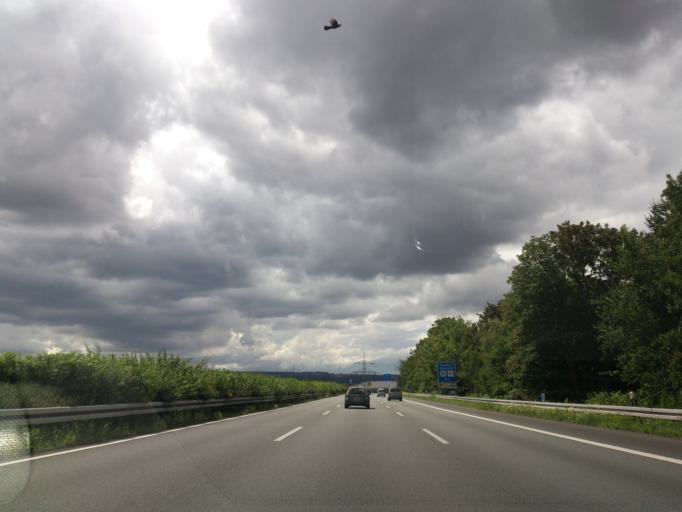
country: DE
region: Lower Saxony
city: Rodenberg
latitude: 52.2930
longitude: 9.3622
